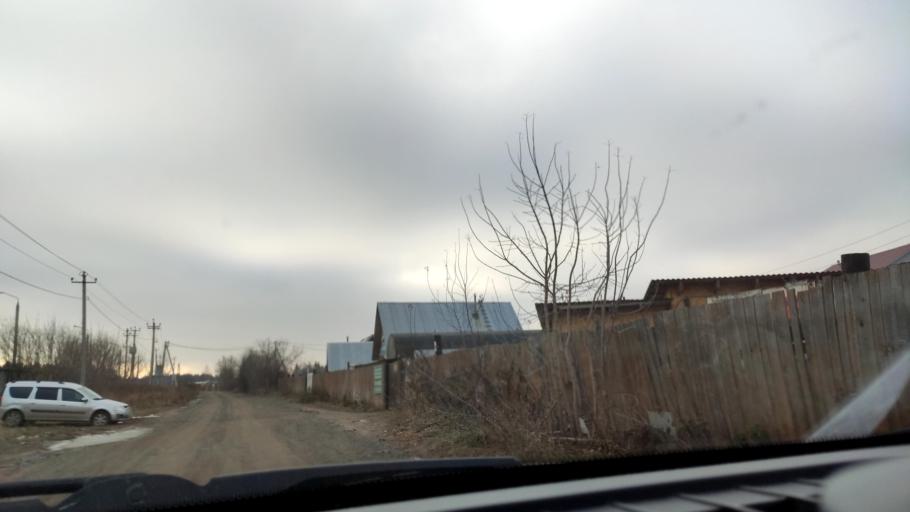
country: RU
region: Perm
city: Kondratovo
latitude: 57.9554
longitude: 56.1714
